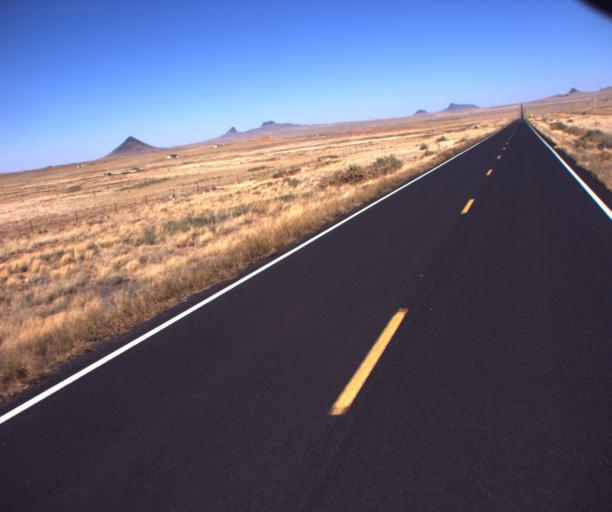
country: US
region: Arizona
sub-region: Navajo County
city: Dilkon
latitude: 35.3109
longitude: -110.4227
